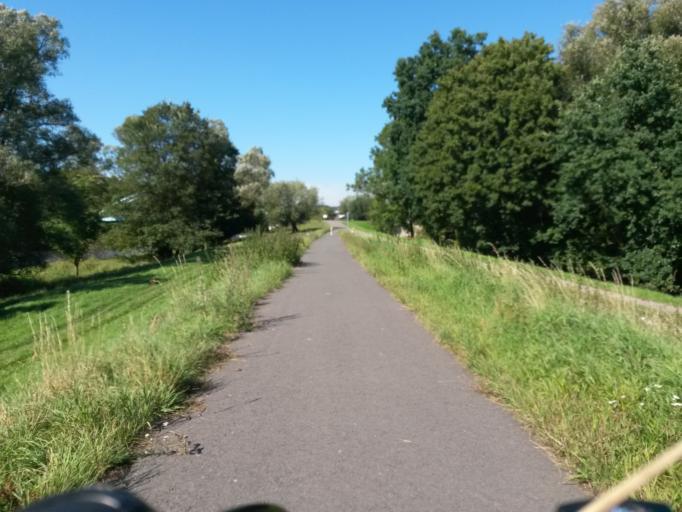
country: DE
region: Brandenburg
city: Schoneberg
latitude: 52.9484
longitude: 14.1107
